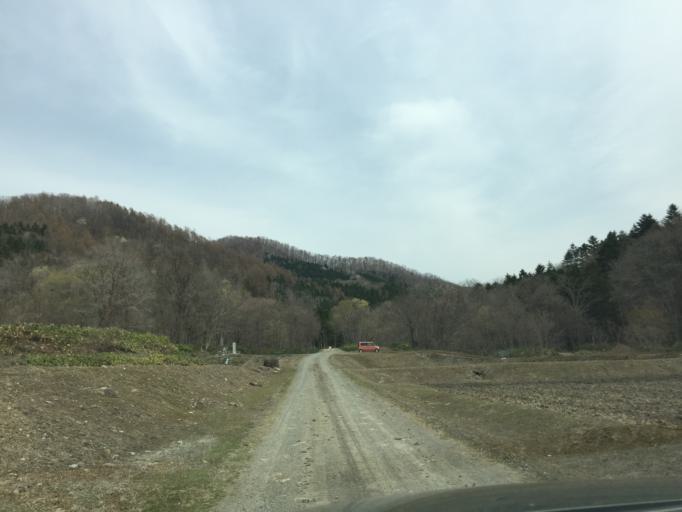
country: JP
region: Hokkaido
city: Ashibetsu
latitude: 43.6235
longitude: 142.2267
